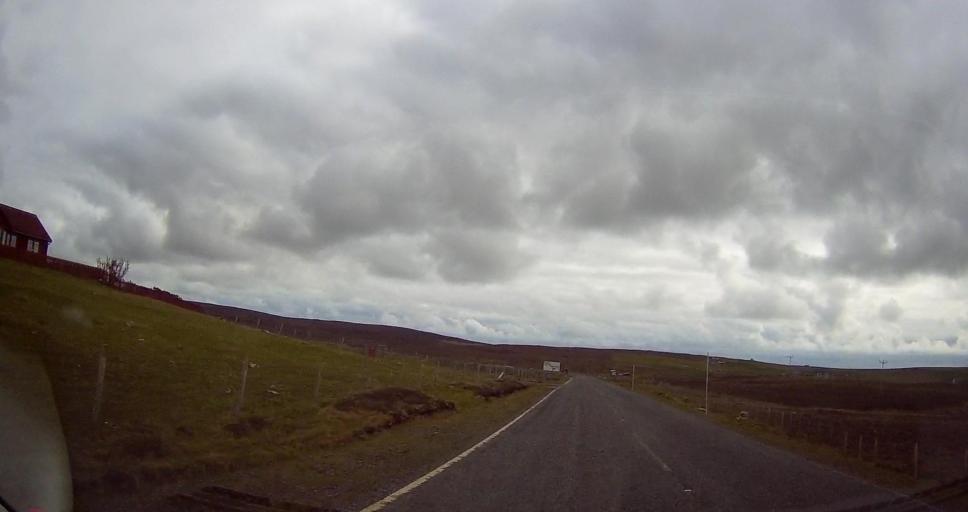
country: GB
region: Scotland
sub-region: Shetland Islands
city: Shetland
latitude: 60.6949
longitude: -0.9295
